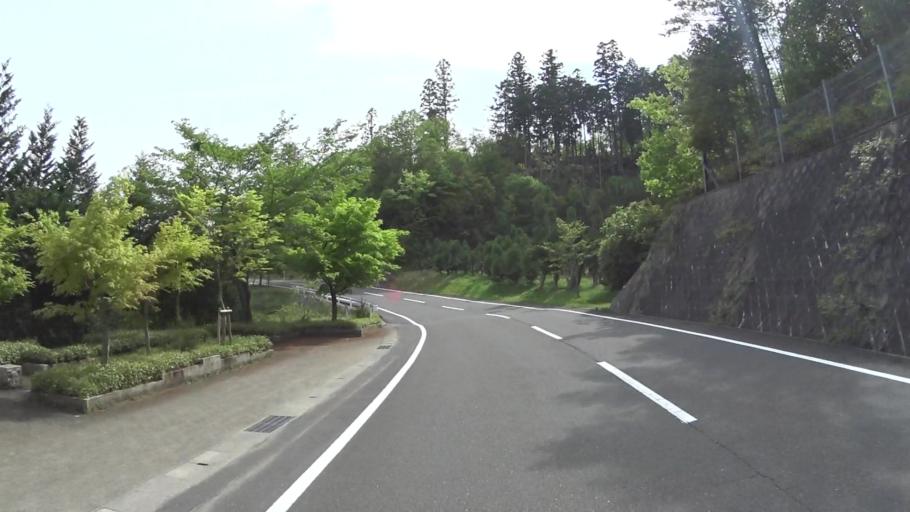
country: JP
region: Kyoto
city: Kameoka
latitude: 35.1495
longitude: 135.6251
